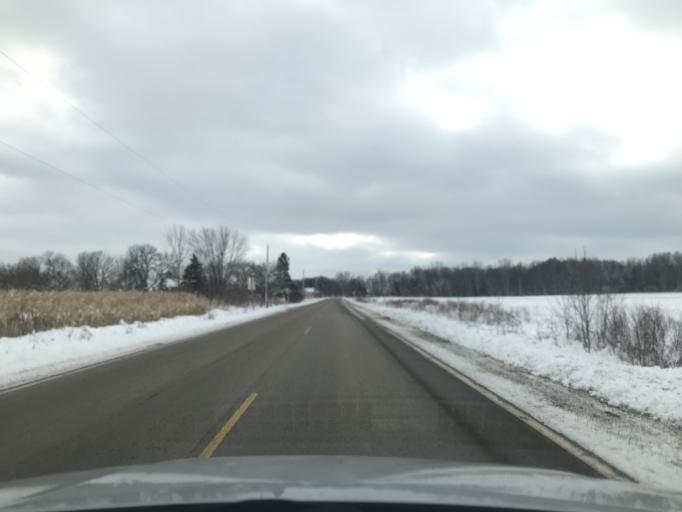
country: US
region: Wisconsin
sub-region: Oconto County
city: Oconto
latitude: 44.9483
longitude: -87.9874
